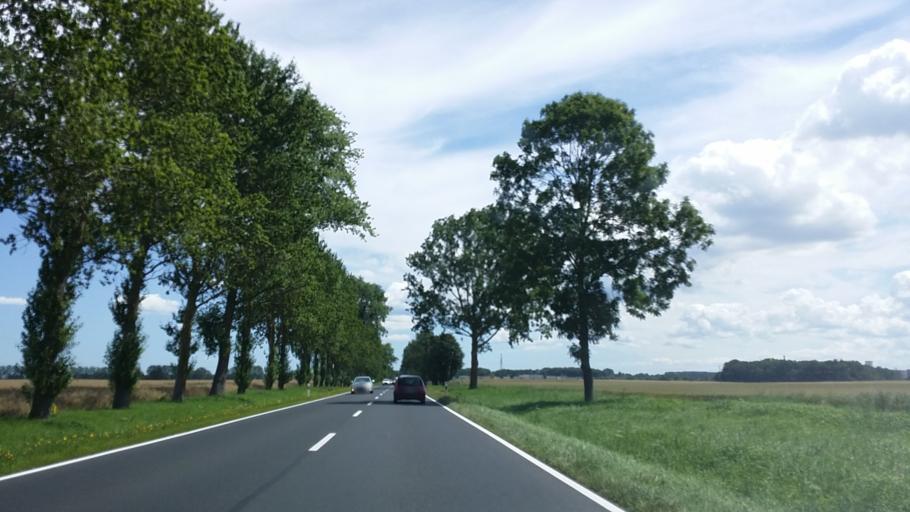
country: PL
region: West Pomeranian Voivodeship
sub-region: Powiat koszalinski
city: Mielno
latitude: 54.2231
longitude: 16.0535
